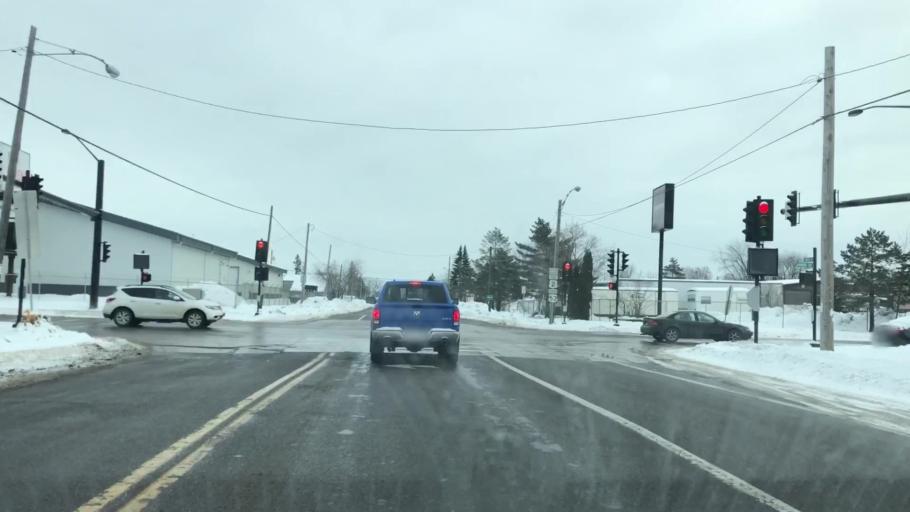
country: US
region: Wisconsin
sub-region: Douglas County
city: Superior
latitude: 46.7279
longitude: -92.0983
